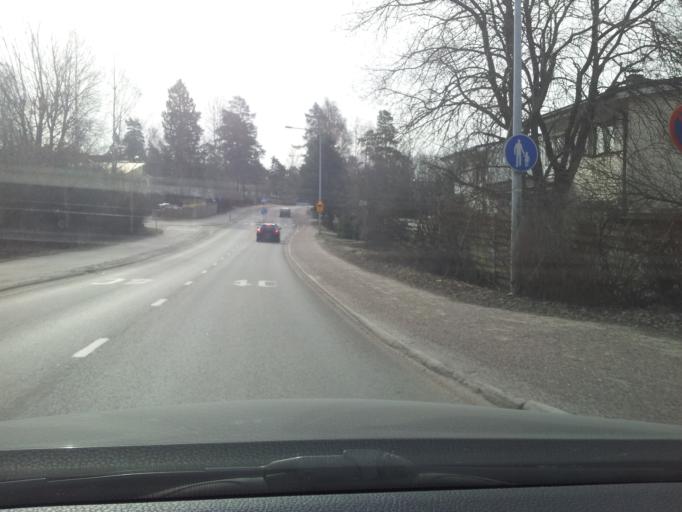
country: FI
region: Uusimaa
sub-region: Helsinki
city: Kilo
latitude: 60.1859
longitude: 24.7855
